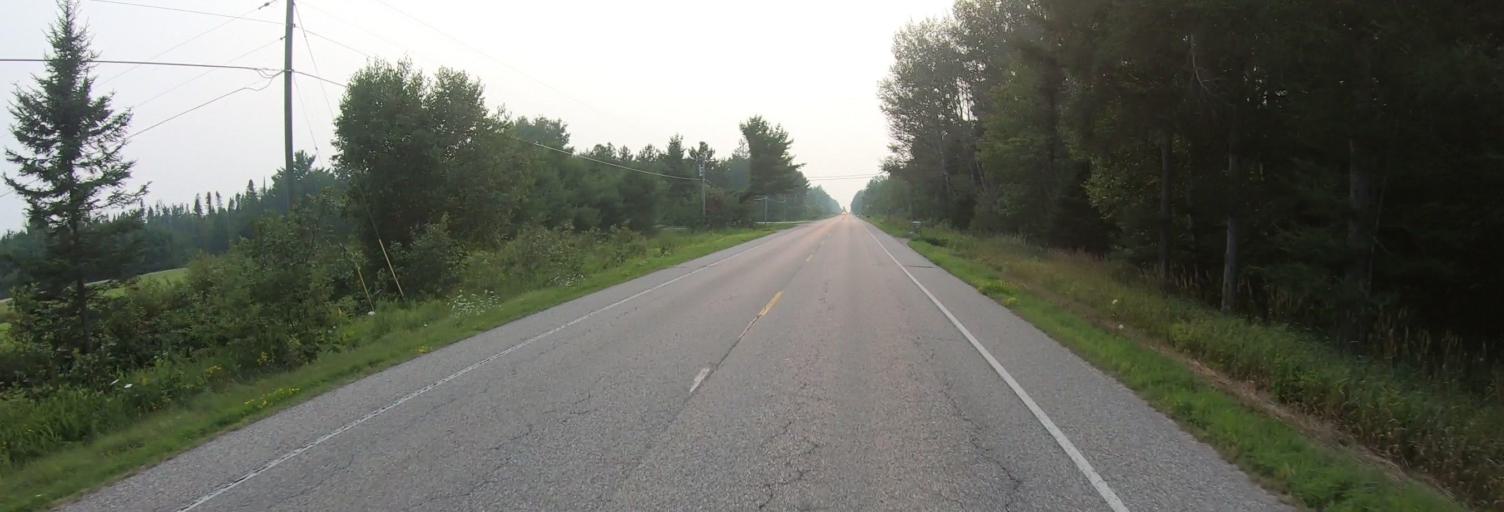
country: US
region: Michigan
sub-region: Chippewa County
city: Sault Ste. Marie
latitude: 46.4188
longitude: -84.4979
